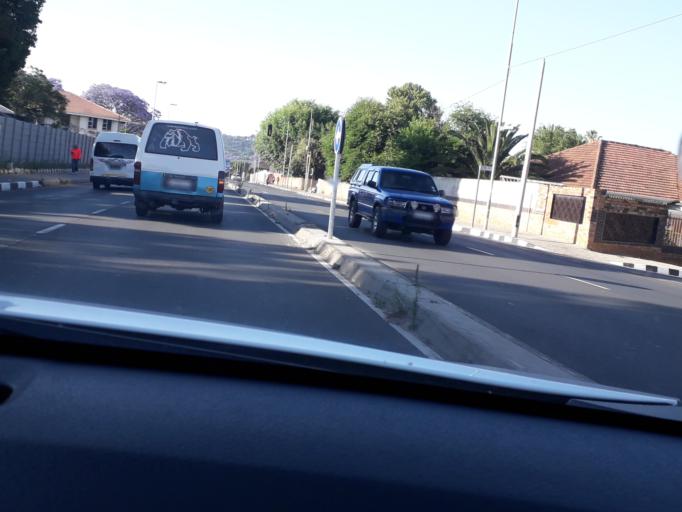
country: ZA
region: Gauteng
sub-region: City of Johannesburg Metropolitan Municipality
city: Johannesburg
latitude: -26.1432
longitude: 28.0867
